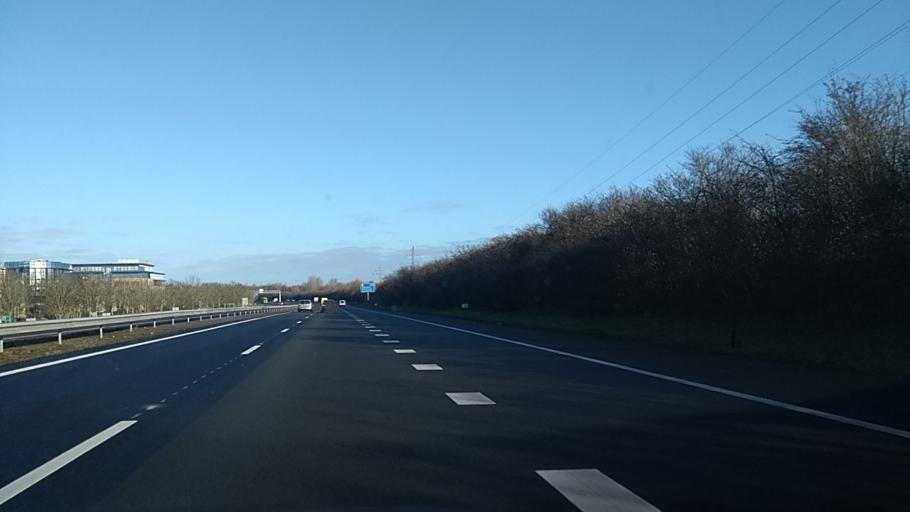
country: NL
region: Drenthe
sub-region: Gemeente Meppel
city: Meppel
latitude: 52.6941
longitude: 6.2078
